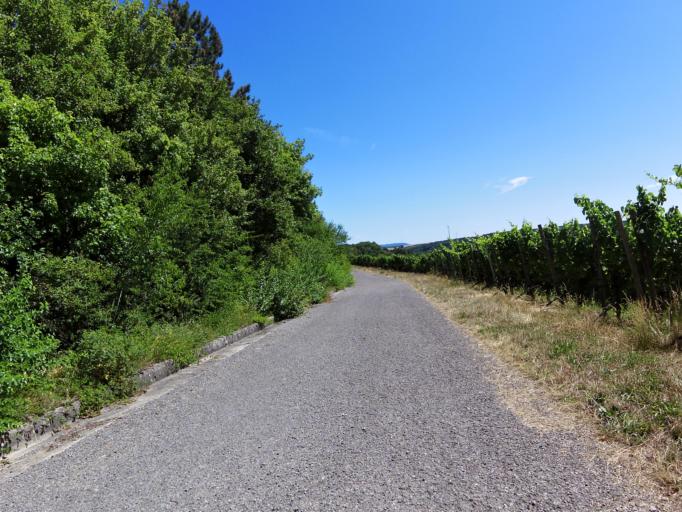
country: DE
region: Bavaria
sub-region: Regierungsbezirk Unterfranken
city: Randersacker
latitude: 49.7582
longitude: 9.9987
